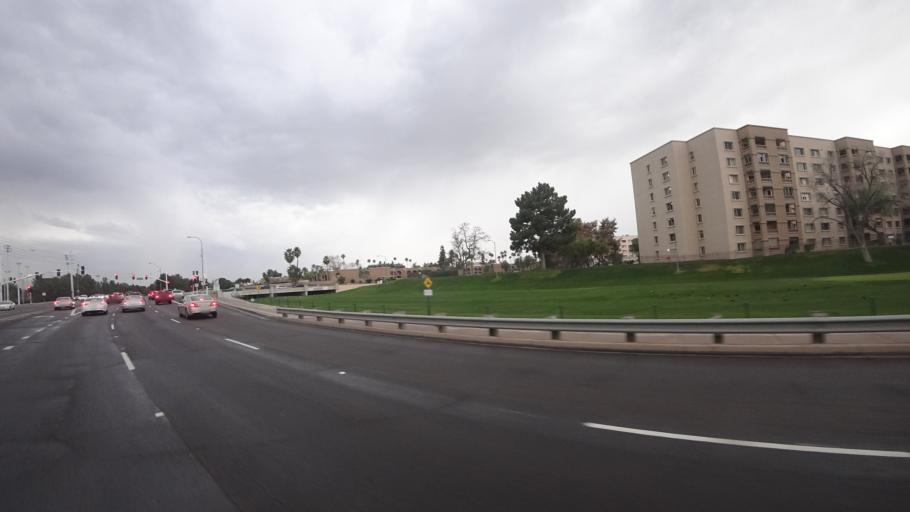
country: US
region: Arizona
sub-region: Maricopa County
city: Scottsdale
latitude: 33.5032
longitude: -111.9088
